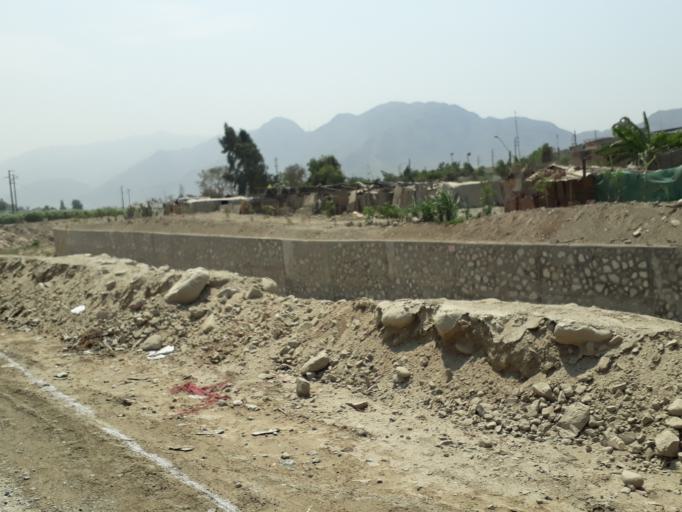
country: PE
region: Lima
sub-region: Lima
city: Santa Maria
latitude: -11.9965
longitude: -76.9134
